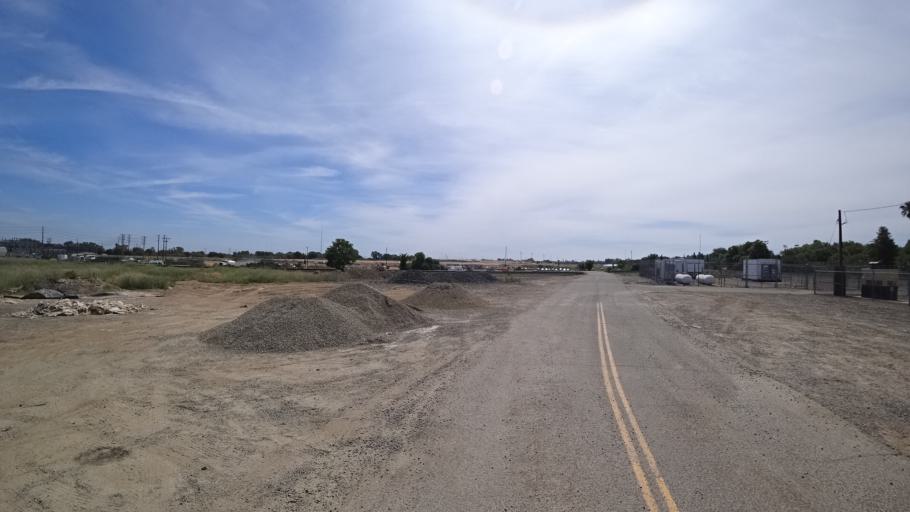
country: US
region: California
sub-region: Sacramento County
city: Sacramento
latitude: 38.5858
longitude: -121.4758
